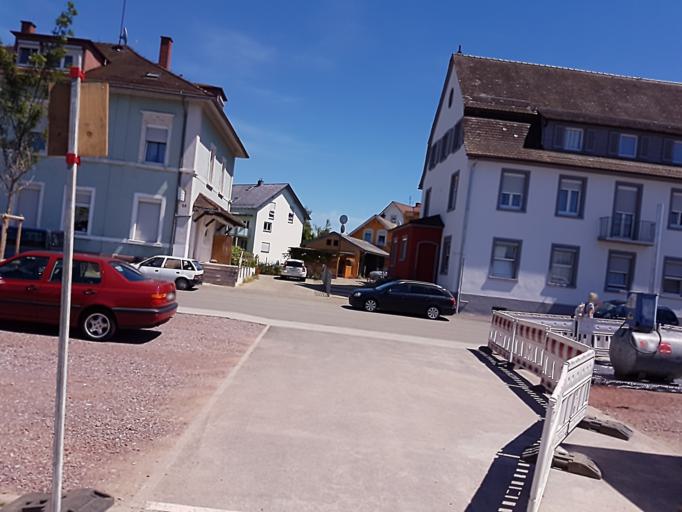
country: DE
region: Baden-Wuerttemberg
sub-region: Freiburg Region
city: Lahr
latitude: 48.3421
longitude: 7.8365
